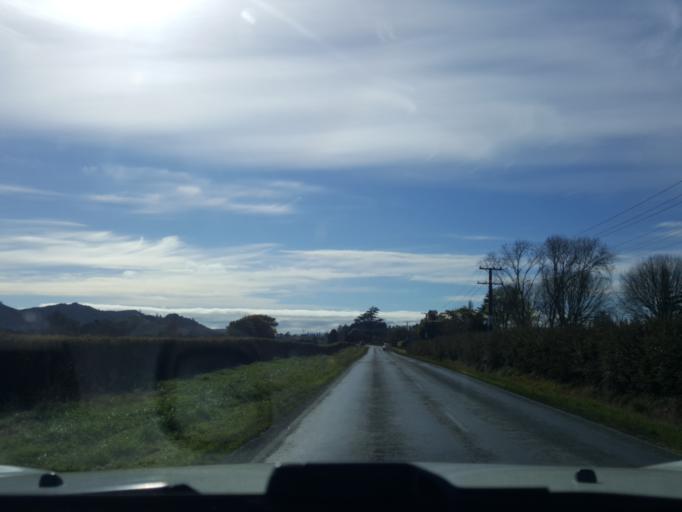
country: NZ
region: Waikato
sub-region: Waikato District
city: Ngaruawahia
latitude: -37.6039
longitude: 175.1998
